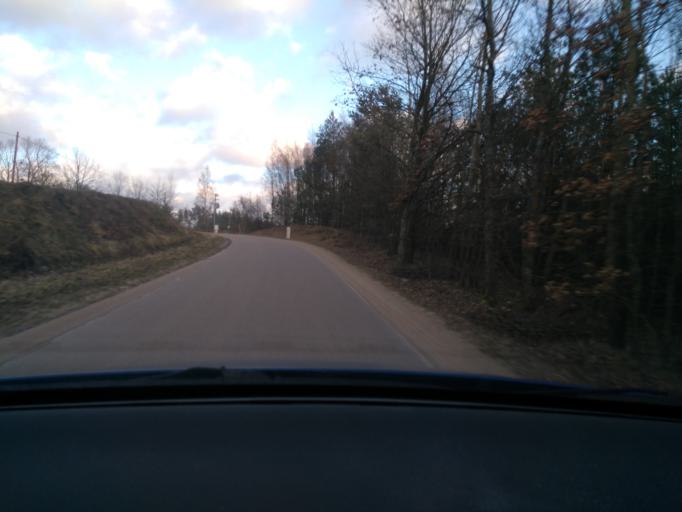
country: PL
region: Pomeranian Voivodeship
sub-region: Powiat kartuski
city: Przodkowo
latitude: 54.4133
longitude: 18.2532
